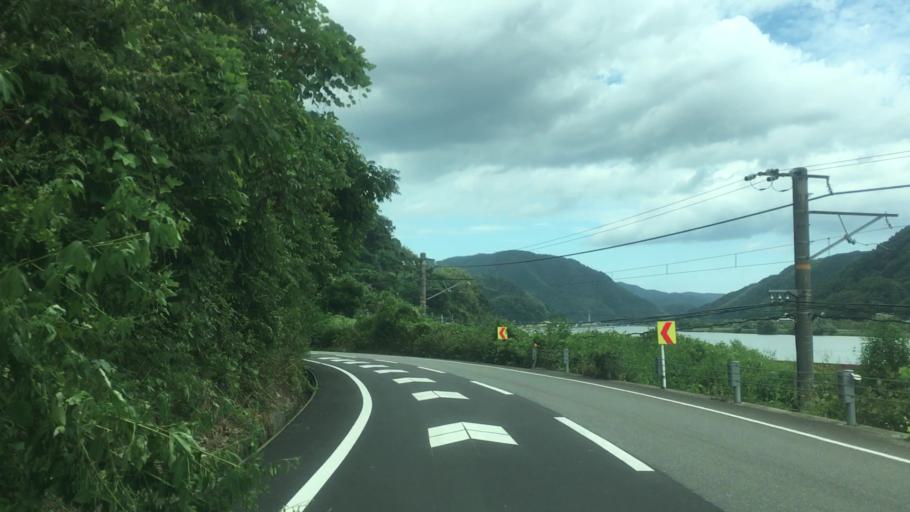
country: JP
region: Hyogo
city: Toyooka
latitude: 35.5796
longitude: 134.7999
